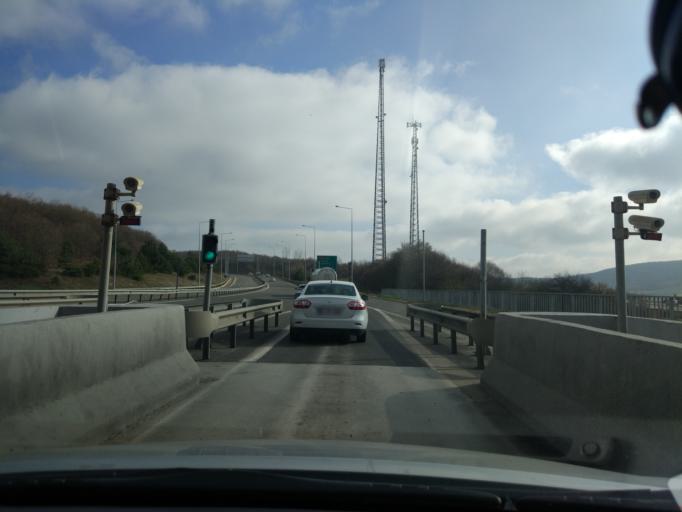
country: TR
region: Bolu
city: Bolu
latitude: 40.7187
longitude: 31.4717
